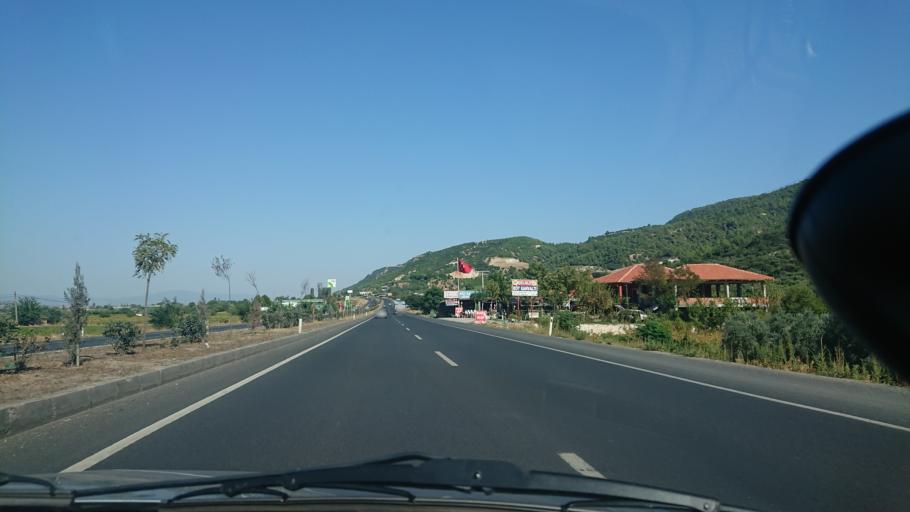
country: TR
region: Manisa
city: Turgutlu
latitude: 38.4833
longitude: 27.8189
